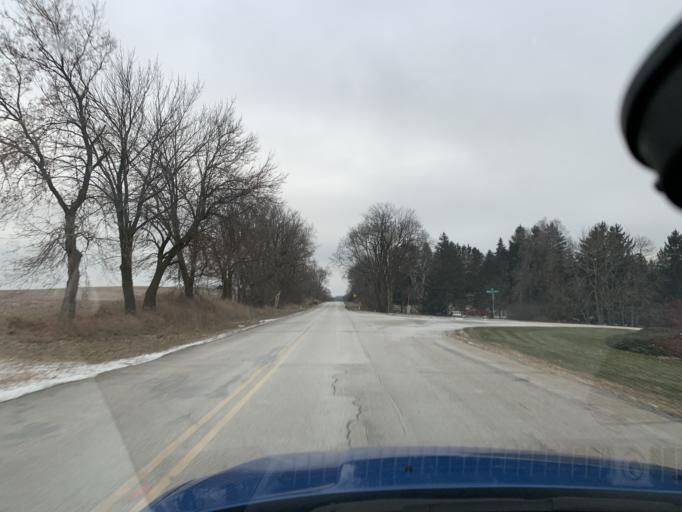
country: US
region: Wisconsin
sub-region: Dane County
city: Middleton
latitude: 43.0708
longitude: -89.5714
